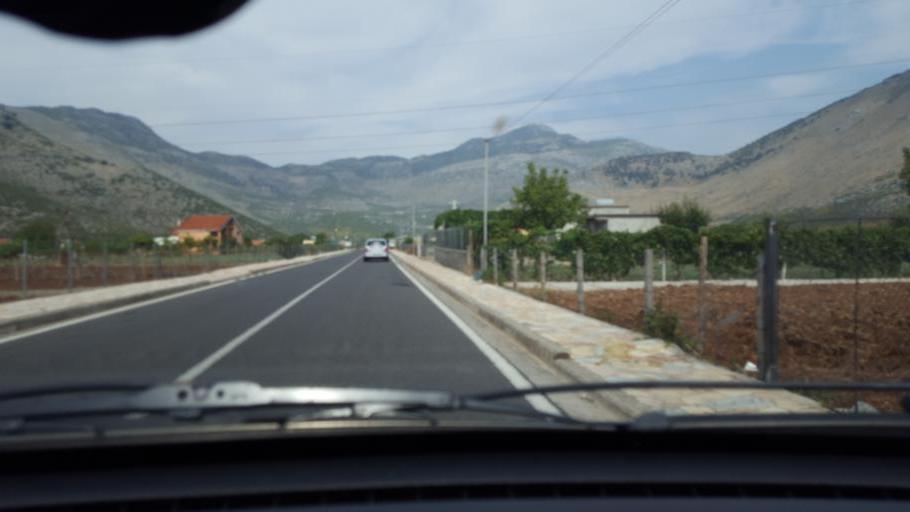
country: AL
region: Shkoder
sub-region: Rrethi i Malesia e Madhe
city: Hot
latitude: 42.3432
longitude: 19.4391
